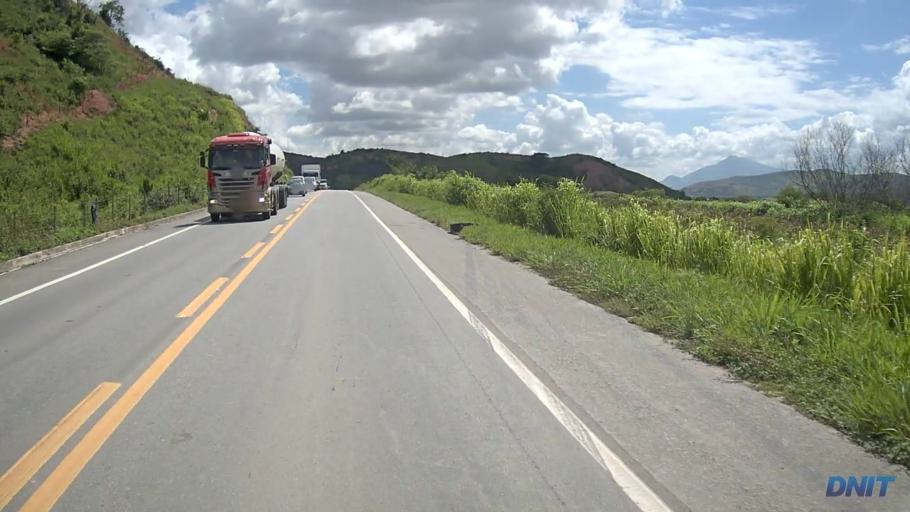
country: BR
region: Minas Gerais
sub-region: Governador Valadares
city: Governador Valadares
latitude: -18.9739
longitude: -42.0960
